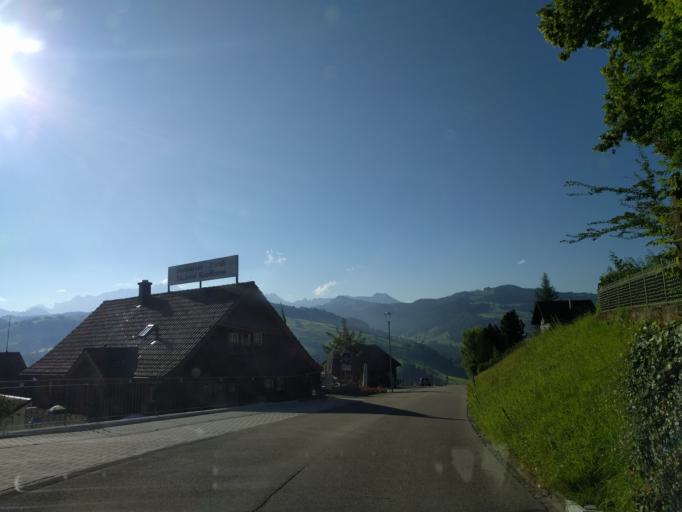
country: CH
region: Saint Gallen
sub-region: Wahlkreis Toggenburg
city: Sankt Peterzell
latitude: 47.3004
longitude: 9.1762
